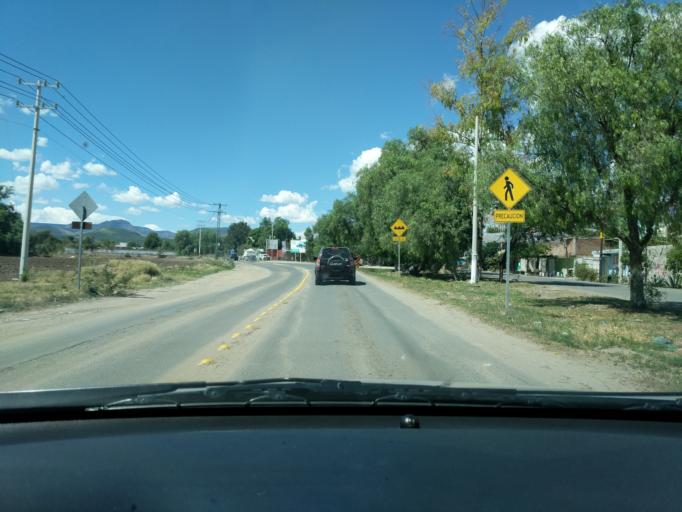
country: MX
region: Guanajuato
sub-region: Leon
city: Ladrilleras del Refugio
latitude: 21.0690
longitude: -101.5509
